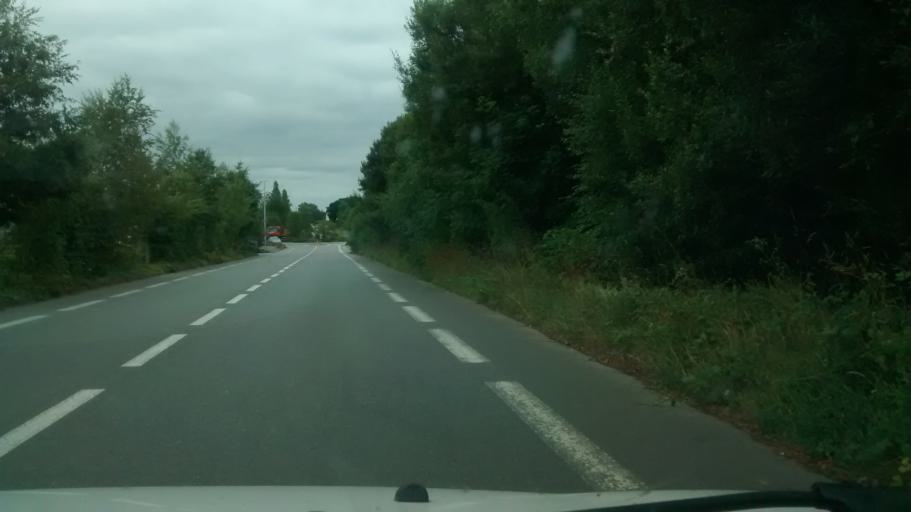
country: FR
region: Brittany
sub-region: Departement du Finistere
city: Plougastel-Daoulas
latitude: 48.3681
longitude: -4.3742
